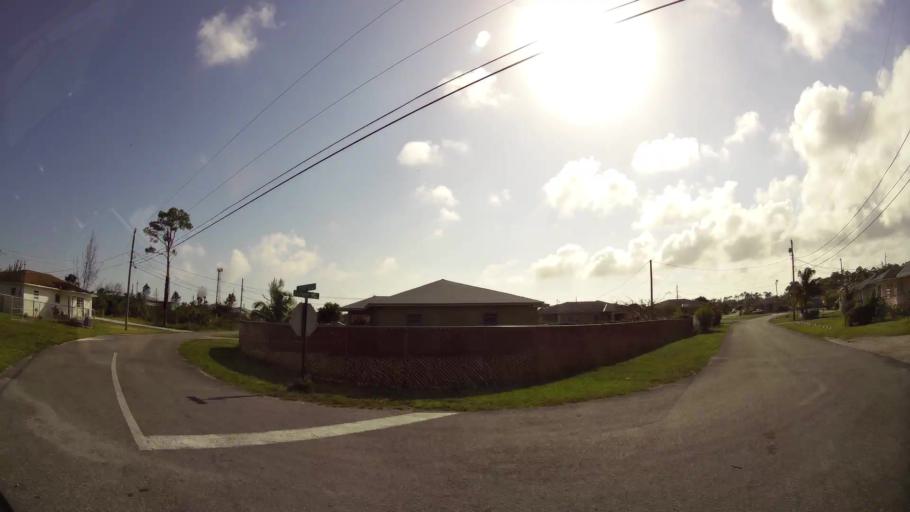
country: BS
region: Freeport
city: Lucaya
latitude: 26.5233
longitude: -78.6651
